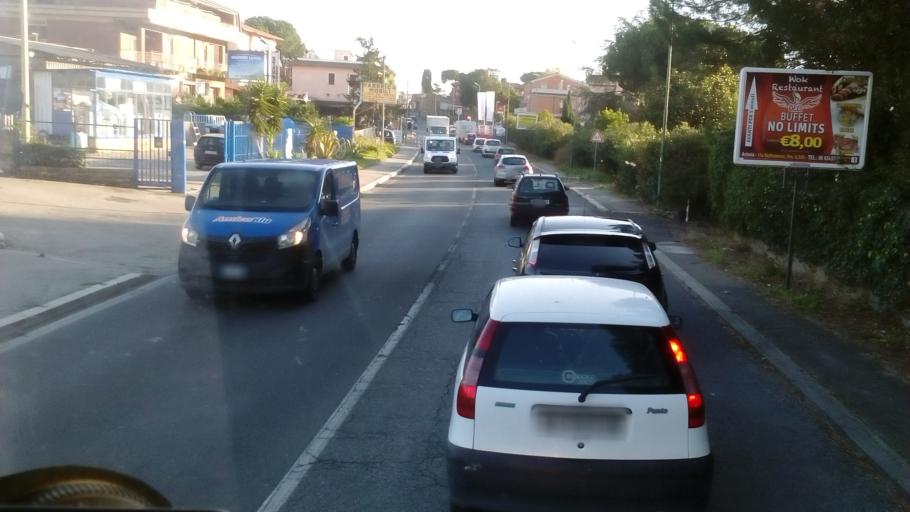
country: IT
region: Latium
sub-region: Citta metropolitana di Roma Capitale
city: Pavona
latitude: 41.7290
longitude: 12.6166
